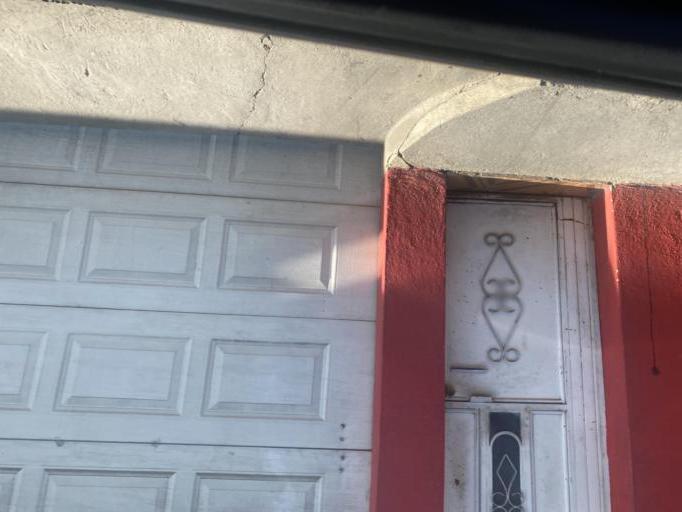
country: GT
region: Quetzaltenango
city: Quetzaltenango
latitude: 14.8555
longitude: -91.5194
